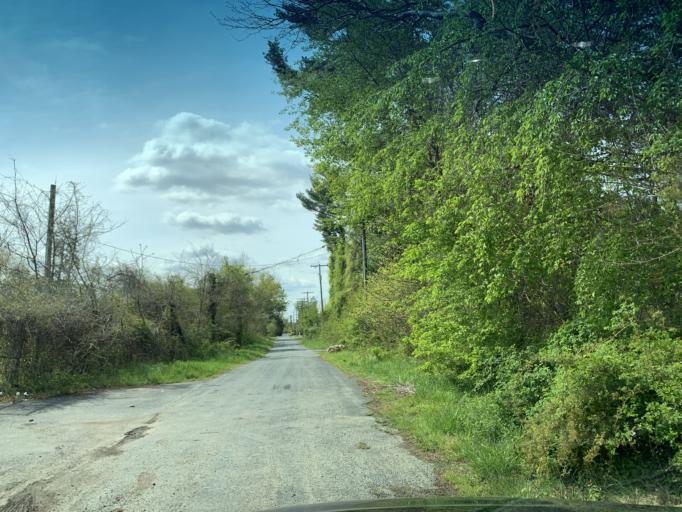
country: US
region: Maryland
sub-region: Harford County
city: Perryman
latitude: 39.4629
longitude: -76.1969
